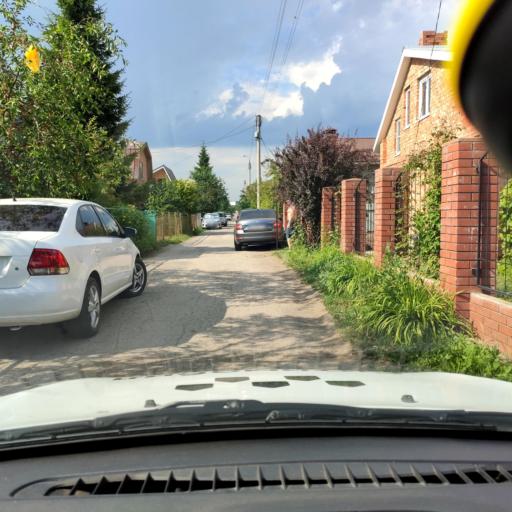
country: RU
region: Samara
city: Podstepki
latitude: 53.5038
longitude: 49.1440
